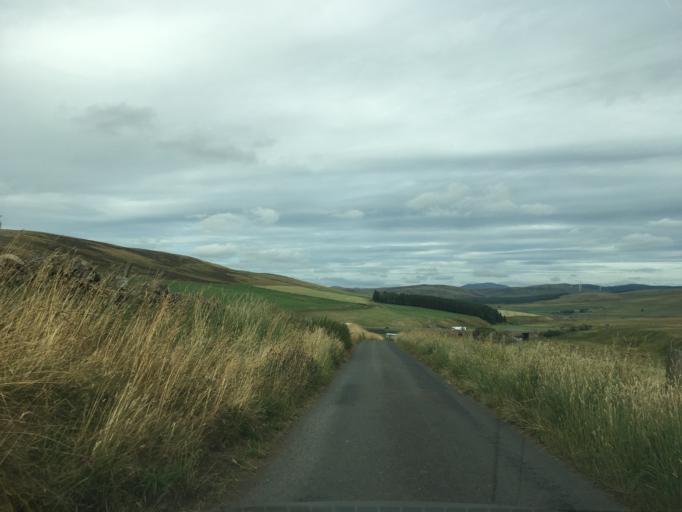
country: GB
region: Scotland
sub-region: South Lanarkshire
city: Douglas
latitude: 55.5136
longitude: -3.7232
